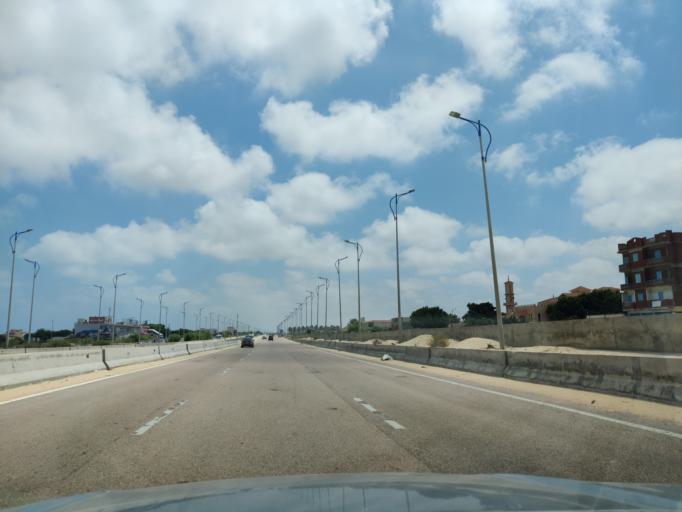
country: EG
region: Alexandria
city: Alexandria
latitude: 30.9758
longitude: 29.5712
